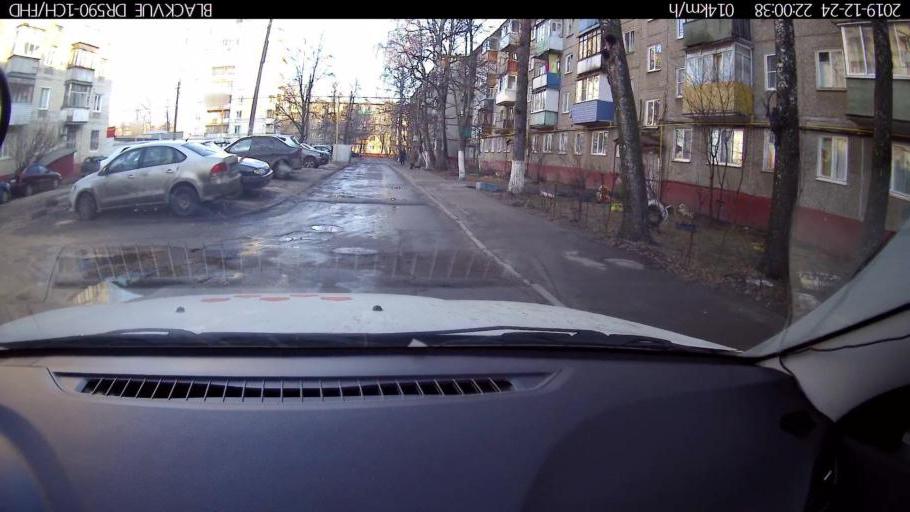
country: RU
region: Nizjnij Novgorod
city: Burevestnik
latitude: 56.2267
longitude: 43.8655
